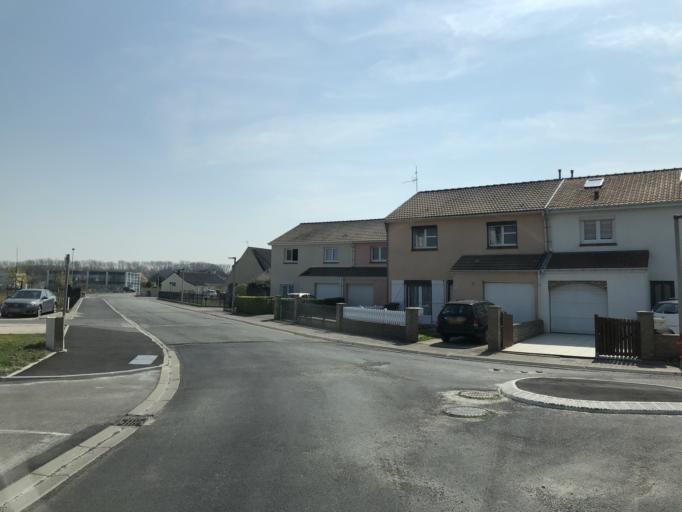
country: FR
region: Nord-Pas-de-Calais
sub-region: Departement du Pas-de-Calais
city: Coquelles
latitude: 50.9439
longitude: 1.8011
